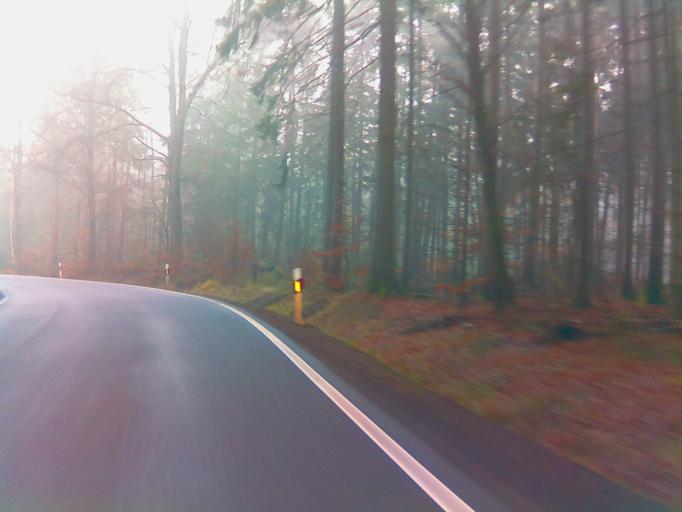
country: DE
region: Hesse
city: Michelstadt
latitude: 49.6958
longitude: 9.0864
